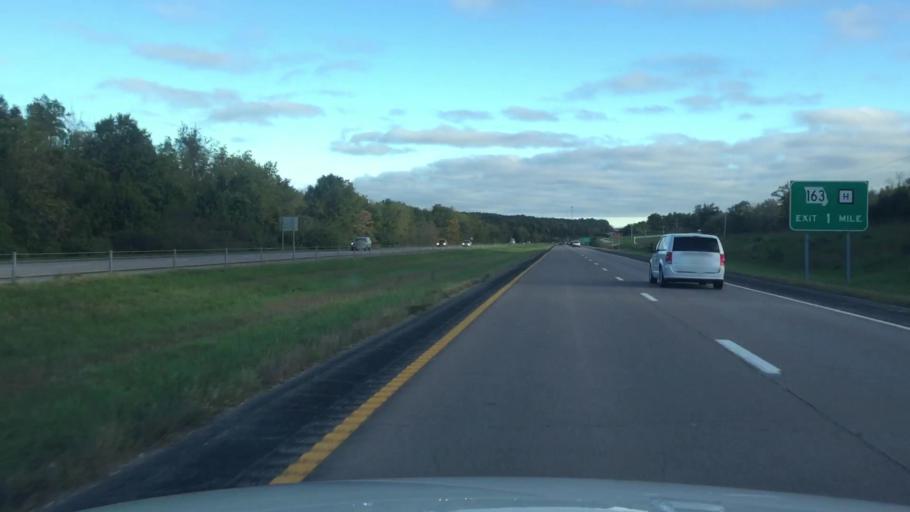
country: US
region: Missouri
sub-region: Boone County
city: Ashland
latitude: 38.8143
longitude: -92.2513
